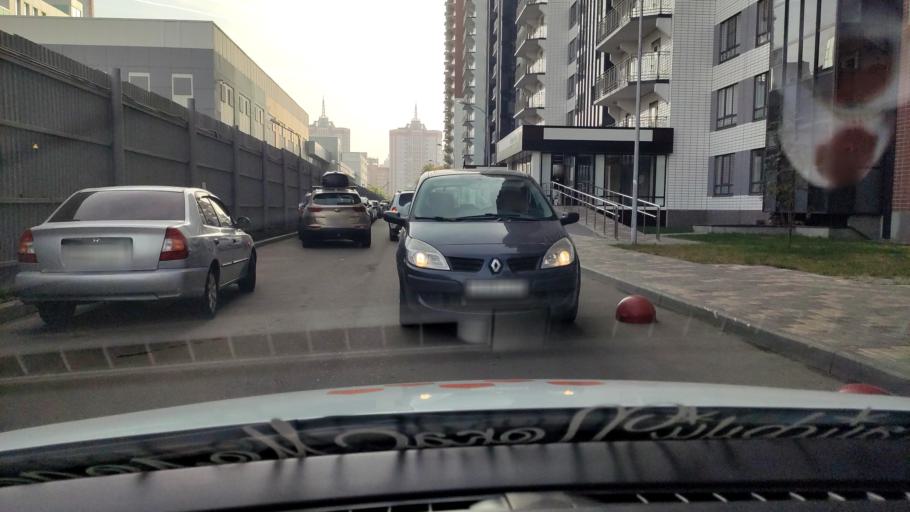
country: RU
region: Voronezj
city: Voronezh
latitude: 51.6681
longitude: 39.1778
